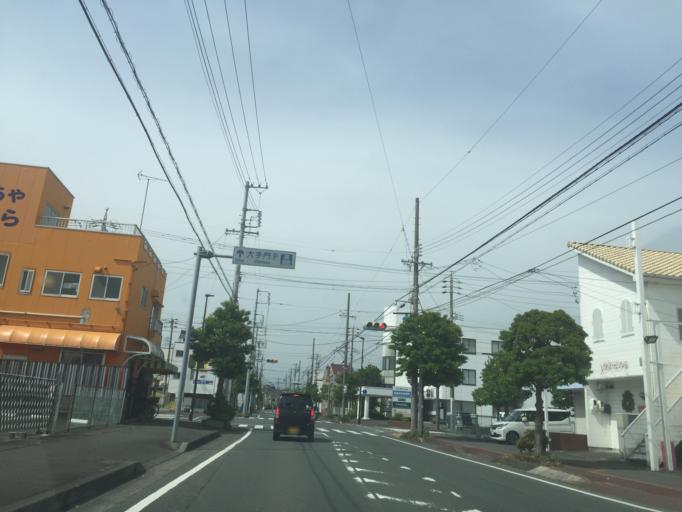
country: JP
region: Shizuoka
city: Kakegawa
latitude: 34.7711
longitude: 138.0187
